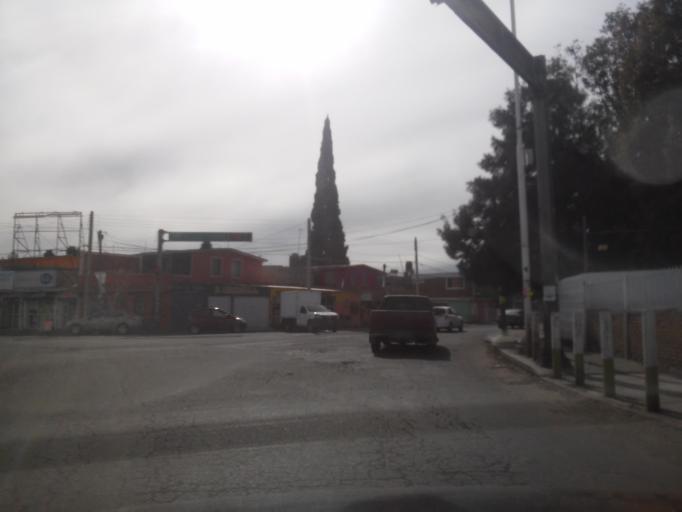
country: MX
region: Durango
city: Victoria de Durango
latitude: 24.0084
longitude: -104.6550
